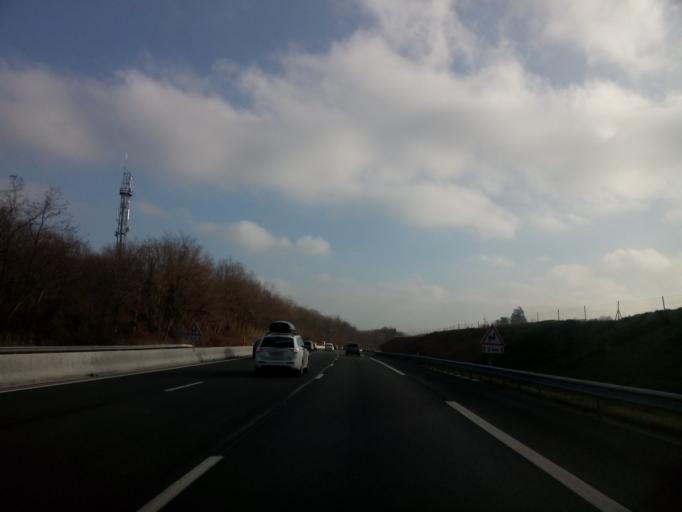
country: FR
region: Rhone-Alpes
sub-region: Departement de l'Isere
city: La Tour-du-Pin
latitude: 45.5591
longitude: 5.4477
